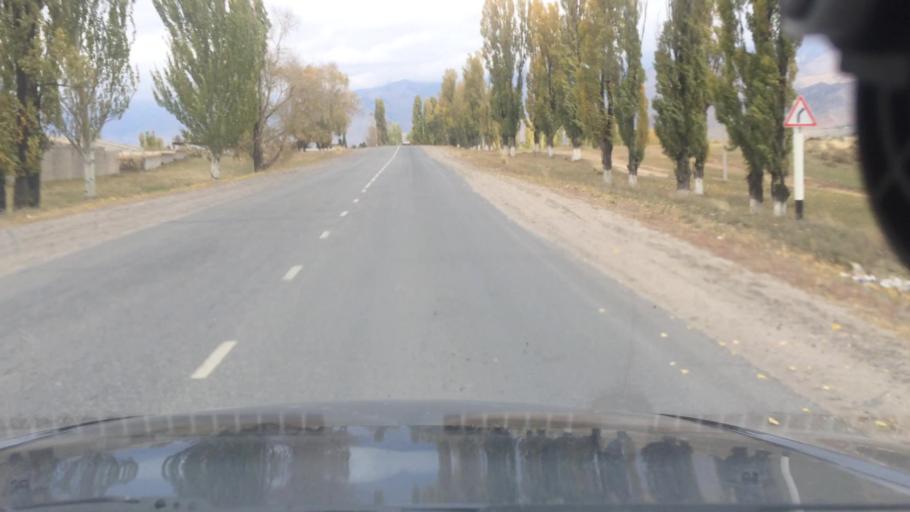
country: KG
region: Ysyk-Koel
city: Tyup
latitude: 42.7411
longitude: 78.3423
